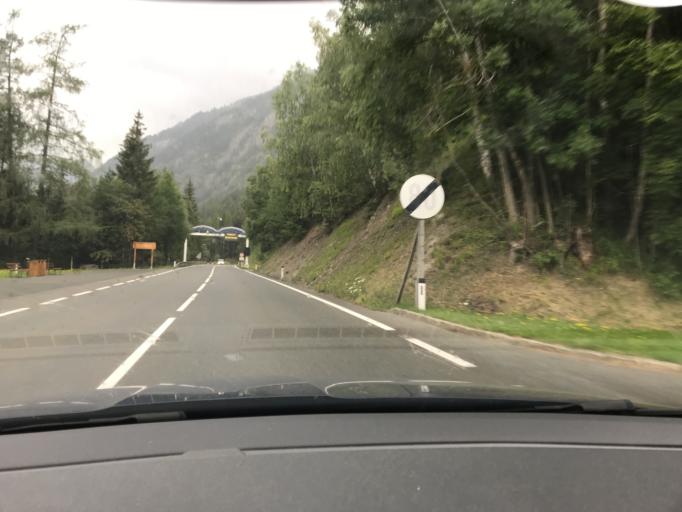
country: AT
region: Tyrol
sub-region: Politischer Bezirk Lienz
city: Matrei in Osttirol
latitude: 47.0106
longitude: 12.5397
